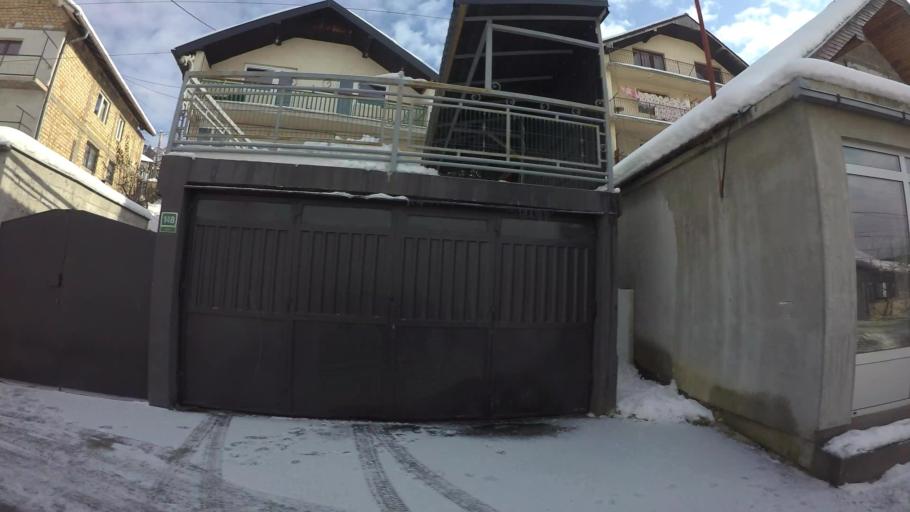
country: BA
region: Federation of Bosnia and Herzegovina
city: Kobilja Glava
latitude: 43.8742
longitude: 18.4195
